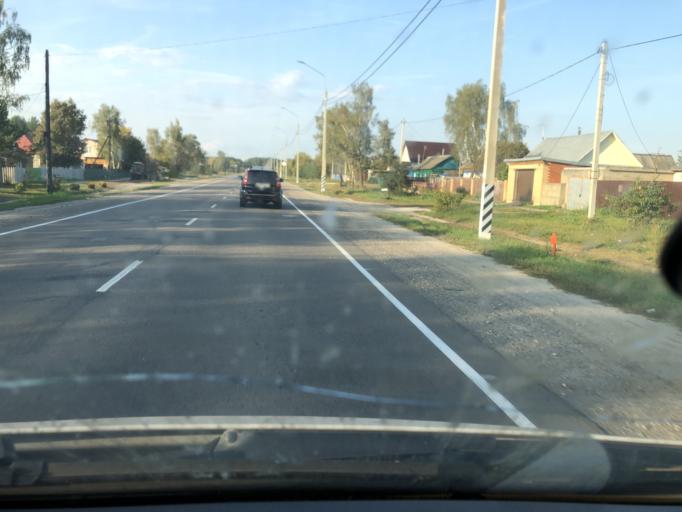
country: RU
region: Kaluga
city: Peremyshl'
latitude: 54.3325
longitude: 36.1814
